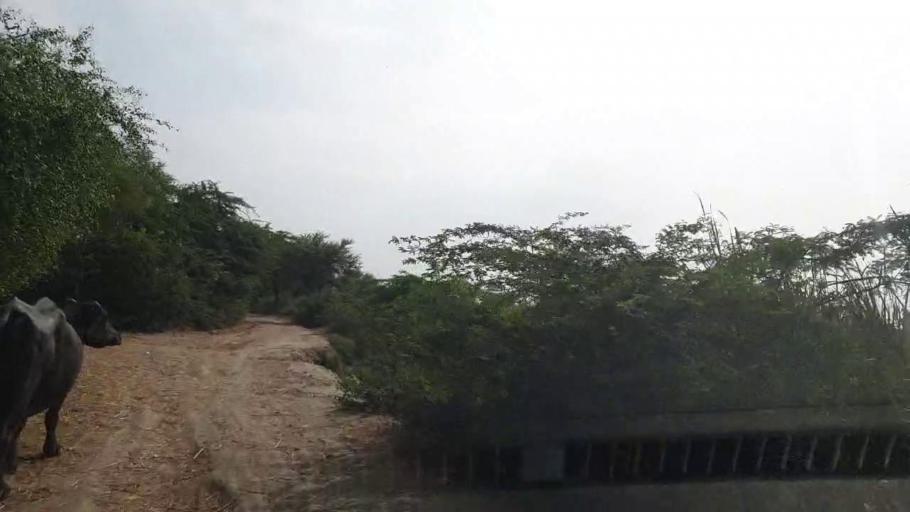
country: PK
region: Sindh
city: Rajo Khanani
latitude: 25.0436
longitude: 68.8025
